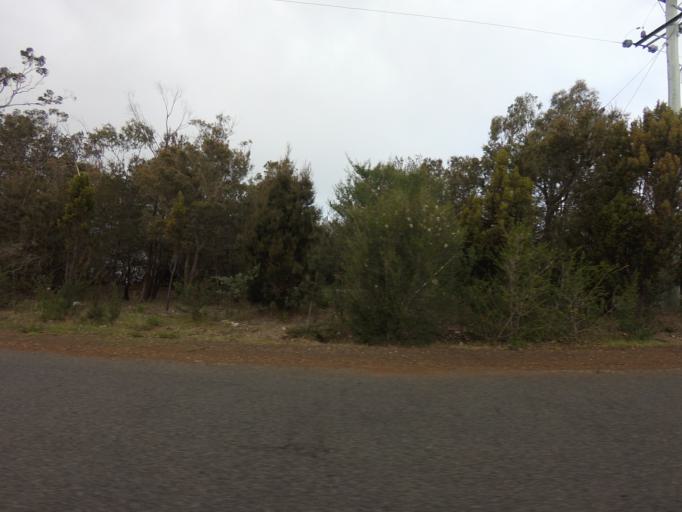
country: AU
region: Tasmania
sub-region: Sorell
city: Sorell
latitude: -42.5326
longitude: 147.9127
